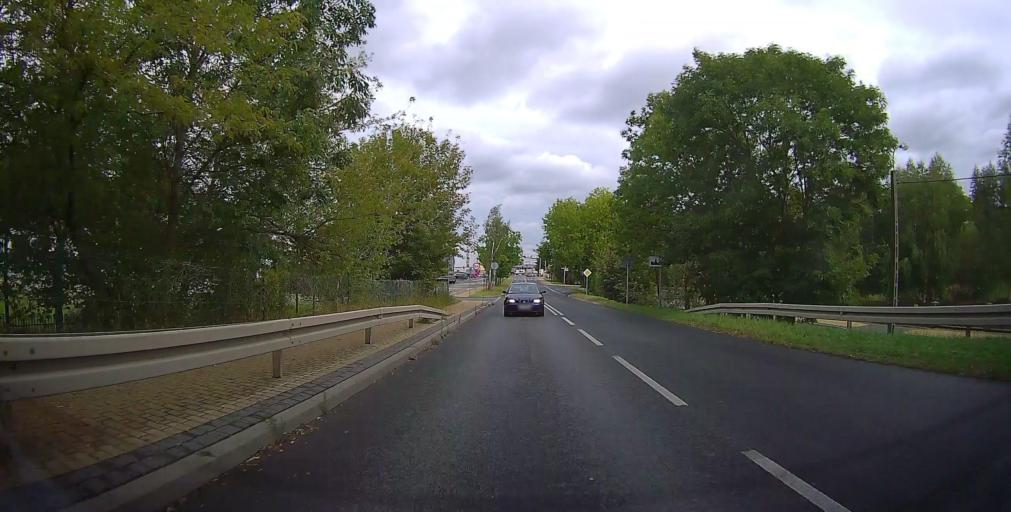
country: PL
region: Masovian Voivodeship
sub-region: Powiat grojecki
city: Grojec
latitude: 51.8626
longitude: 20.8572
